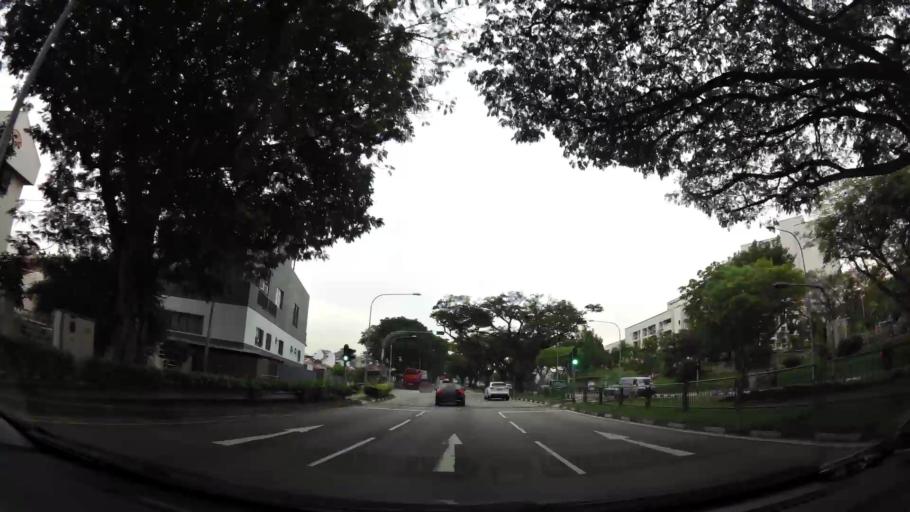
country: SG
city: Singapore
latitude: 1.3666
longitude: 103.8754
